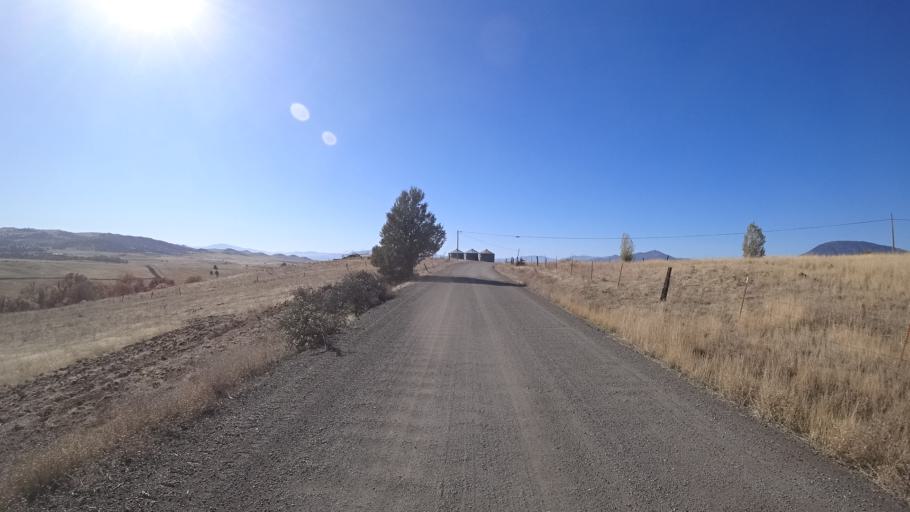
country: US
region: California
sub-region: Siskiyou County
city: Montague
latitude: 41.8308
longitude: -122.3906
